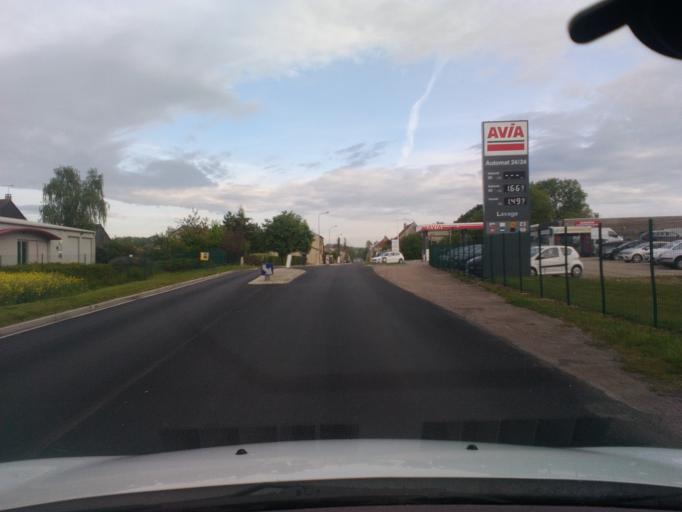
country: FR
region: Champagne-Ardenne
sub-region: Departement de la Haute-Marne
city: Lavilleneuve-au-Roi
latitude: 48.1814
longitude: 4.9827
